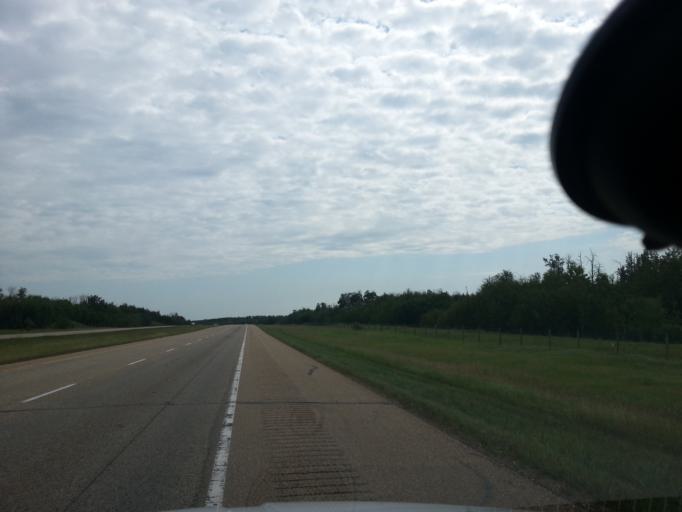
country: CA
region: Alberta
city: Lamont
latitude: 53.5666
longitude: -112.9101
